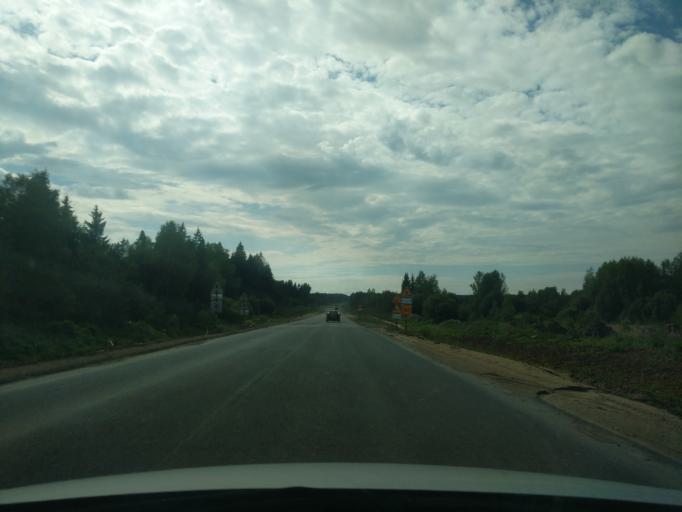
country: RU
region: Kostroma
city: Sudislavl'
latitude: 57.8564
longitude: 41.6064
